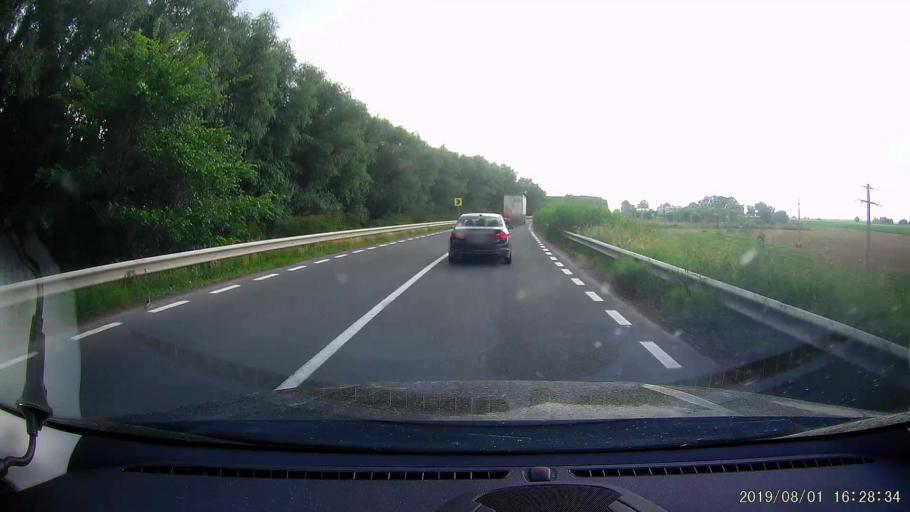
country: BG
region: Silistra
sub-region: Obshtina Silistra
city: Silistra
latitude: 44.1468
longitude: 27.3054
